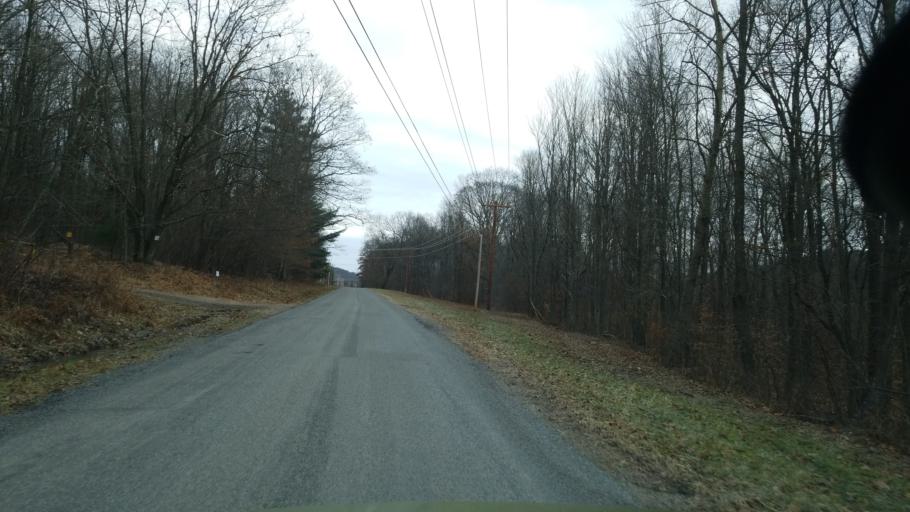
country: US
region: Pennsylvania
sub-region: Clearfield County
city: Treasure Lake
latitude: 41.1147
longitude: -78.6236
